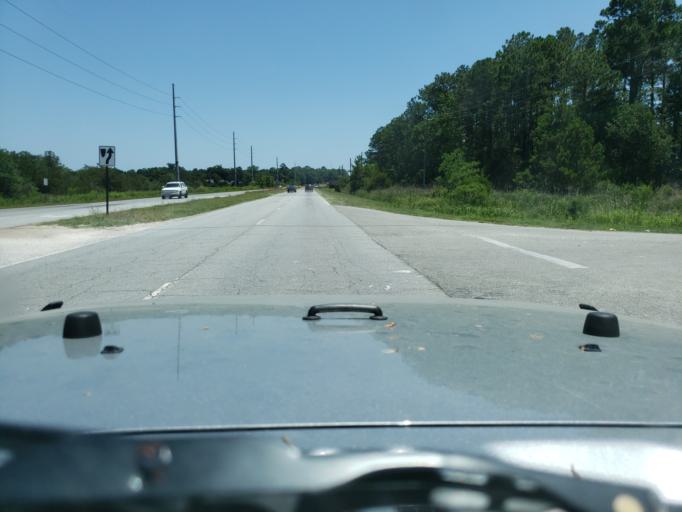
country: US
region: Georgia
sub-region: Chatham County
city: Thunderbolt
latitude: 32.0656
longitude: -81.0408
